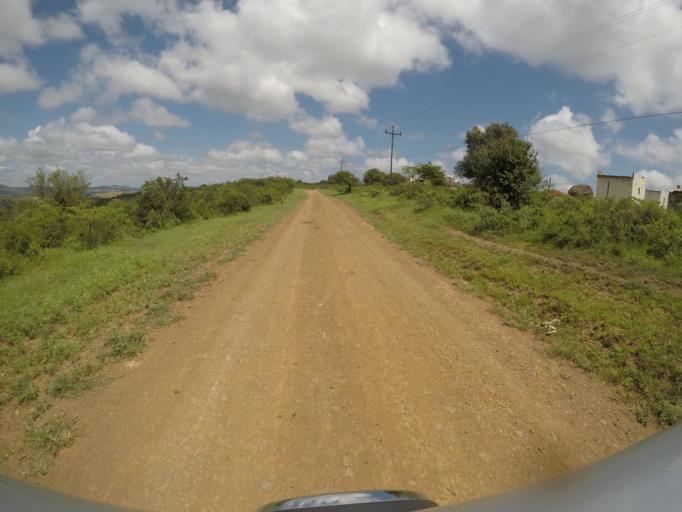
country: ZA
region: KwaZulu-Natal
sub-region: uThungulu District Municipality
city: Empangeni
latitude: -28.5873
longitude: 31.8216
